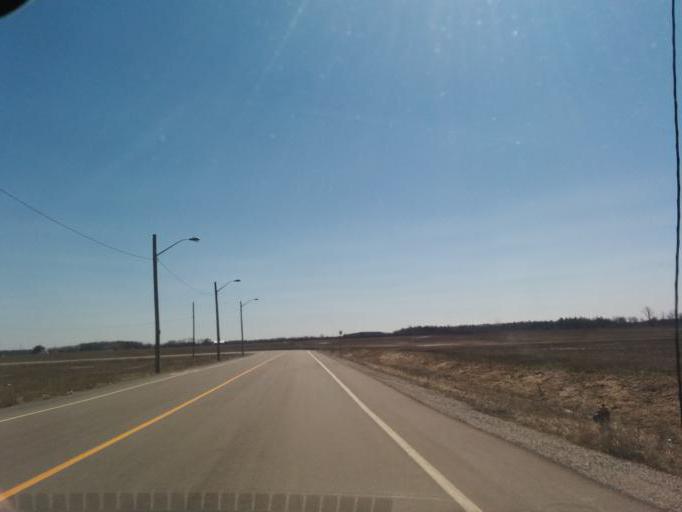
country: CA
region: Ontario
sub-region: Halton
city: Milton
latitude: 43.4746
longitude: -79.8743
